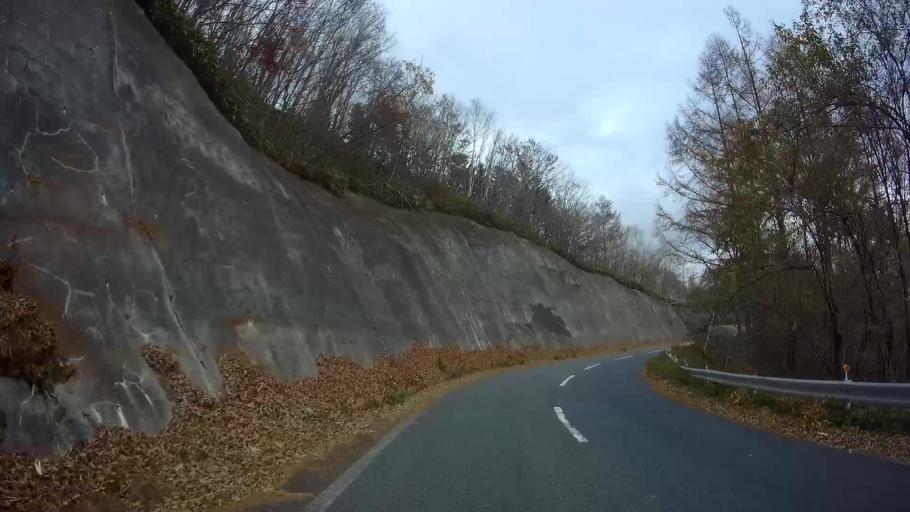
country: JP
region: Gunma
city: Nakanojomachi
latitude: 36.6811
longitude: 138.6626
